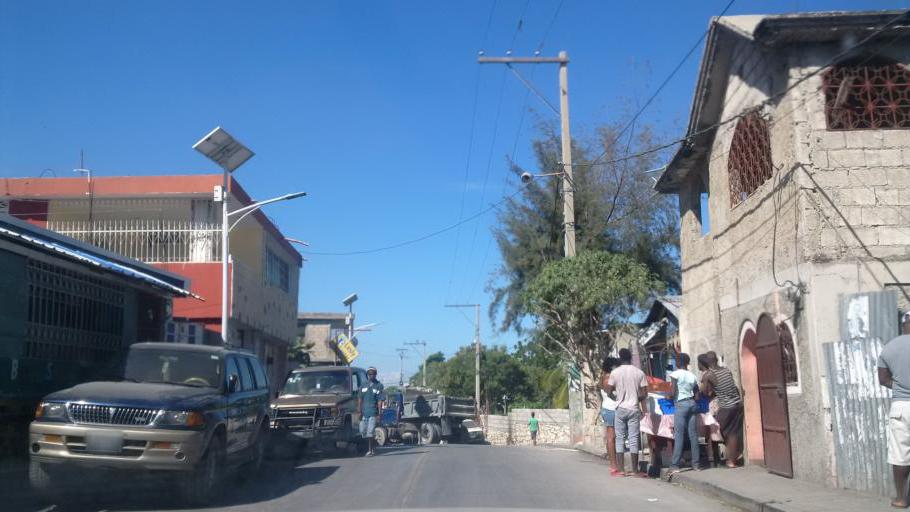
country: HT
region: Ouest
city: Port-au-Prince
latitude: 18.5464
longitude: -72.3197
